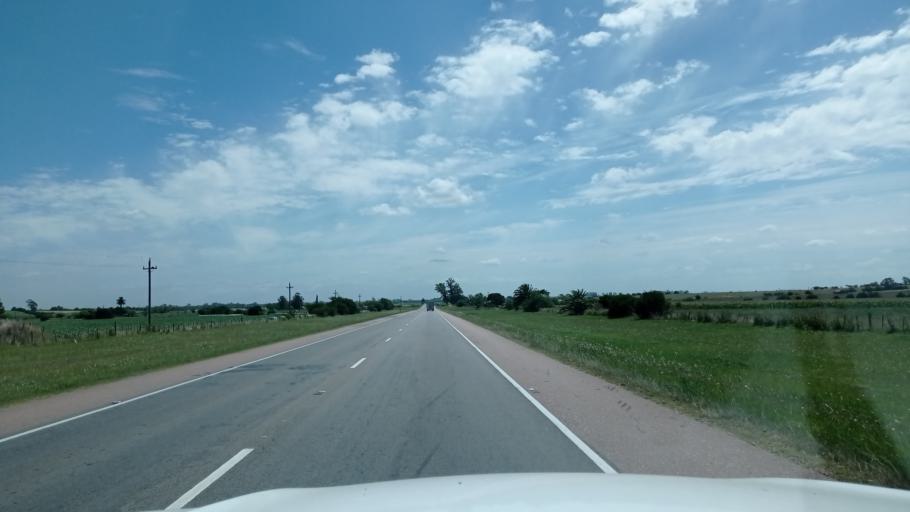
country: UY
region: Canelones
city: Canelones
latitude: -34.3954
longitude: -56.2558
